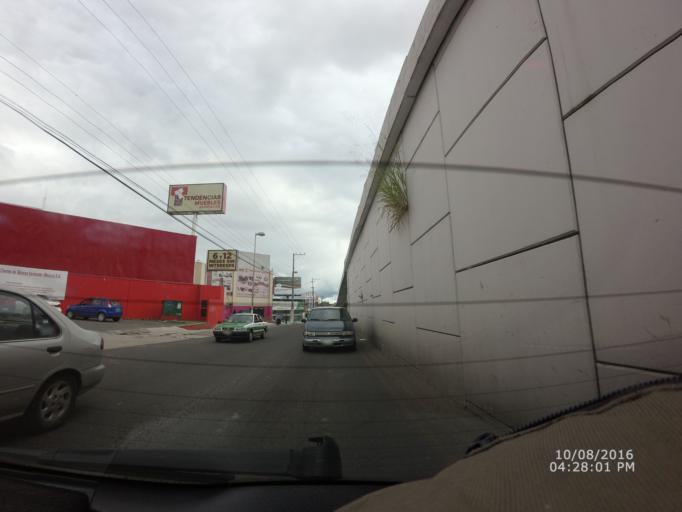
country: MX
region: Veracruz
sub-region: Xalapa
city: Xalapa de Enriquez
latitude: 19.5372
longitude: -96.9077
